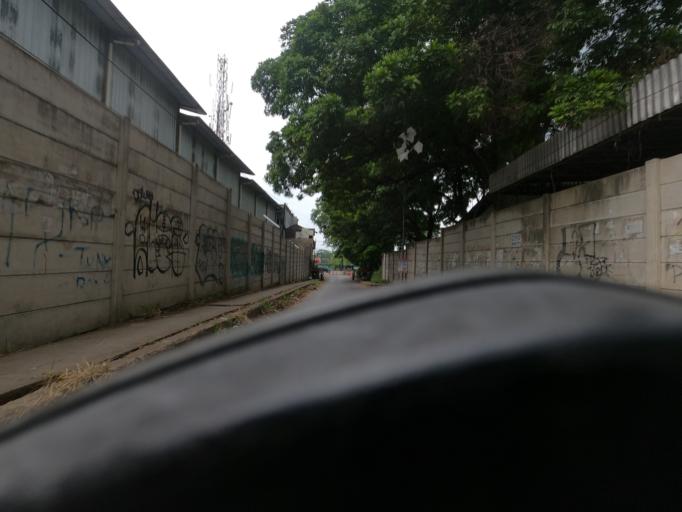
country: ID
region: West Java
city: Padalarang
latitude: -6.8471
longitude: 107.4923
